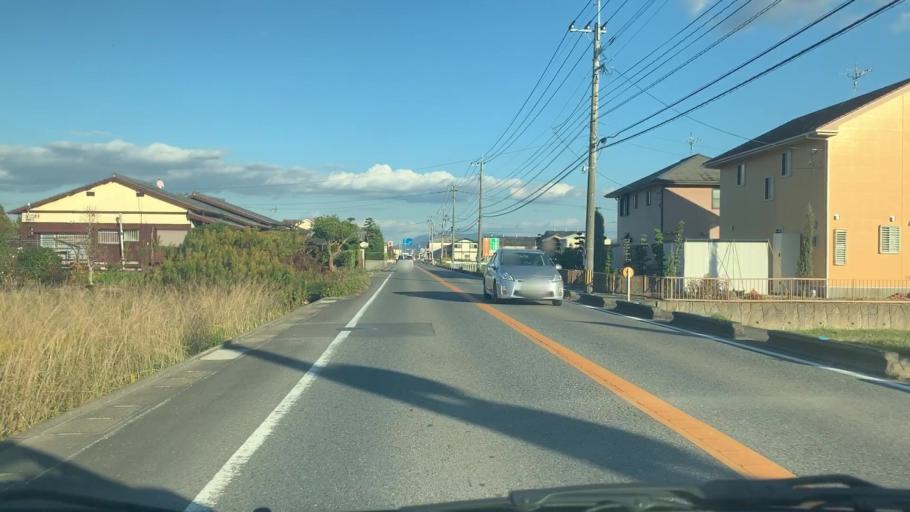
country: JP
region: Saga Prefecture
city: Kanzakimachi-kanzaki
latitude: 33.2973
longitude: 130.4400
